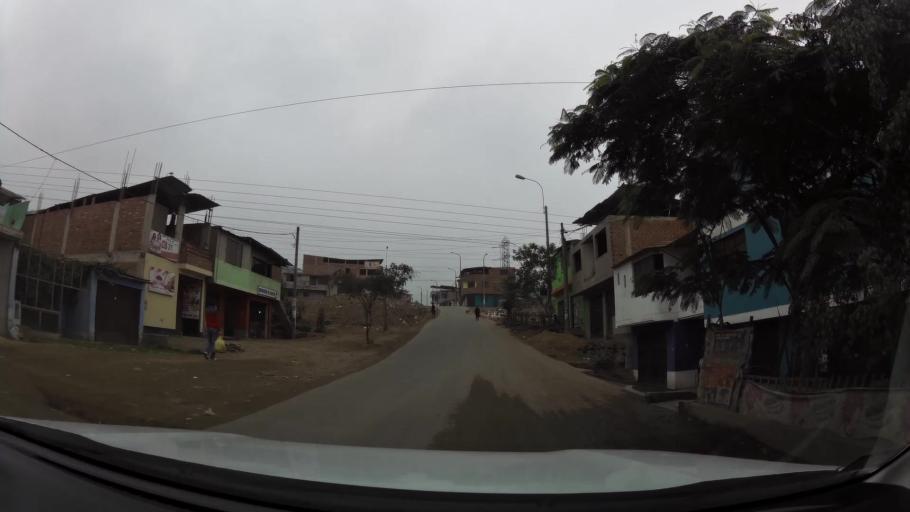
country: PE
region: Lima
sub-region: Lima
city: Surco
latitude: -12.2185
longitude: -76.9199
